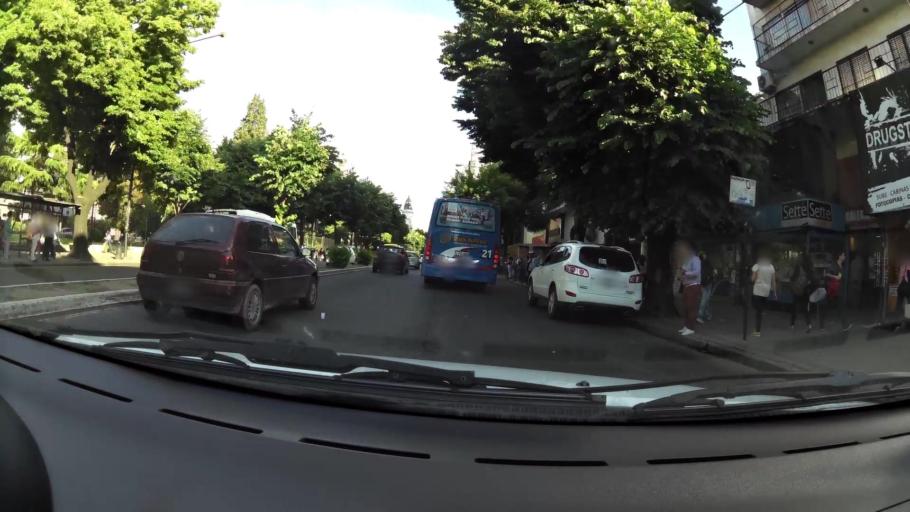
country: AR
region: Buenos Aires
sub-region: Partido de La Plata
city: La Plata
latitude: -34.9127
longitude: -57.9526
